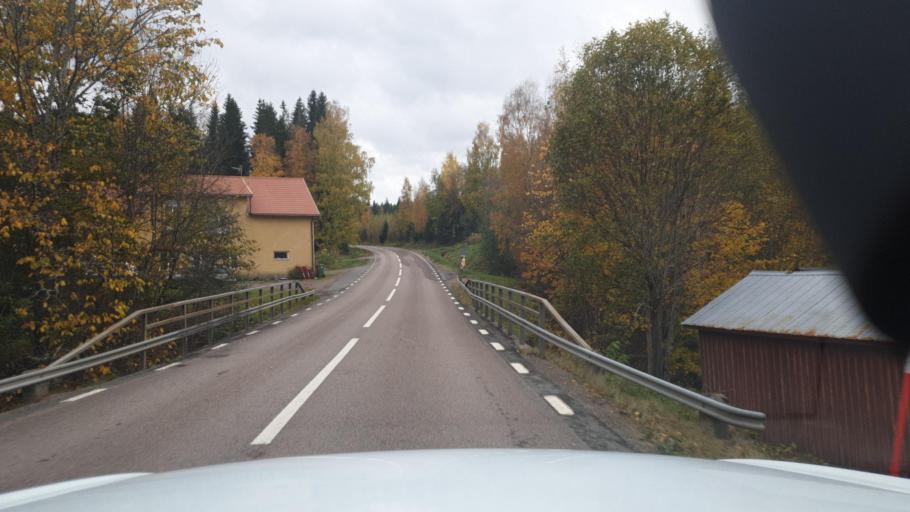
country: SE
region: Vaermland
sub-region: Sunne Kommun
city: Sunne
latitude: 59.9087
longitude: 12.9056
